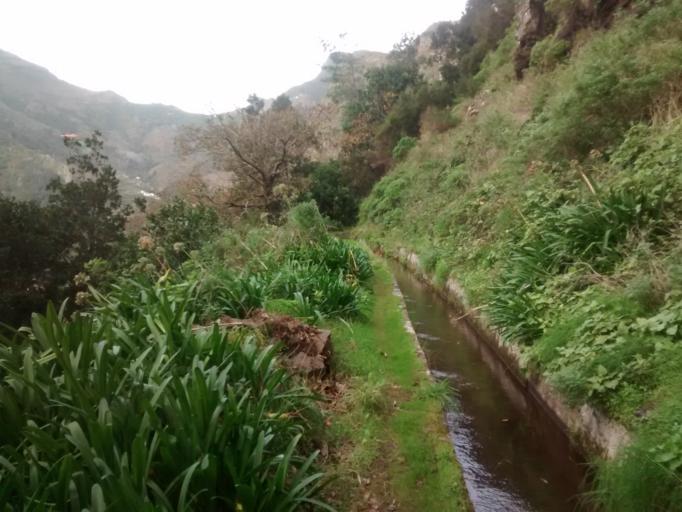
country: PT
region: Madeira
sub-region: Camara de Lobos
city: Curral das Freiras
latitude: 32.7267
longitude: -17.0173
